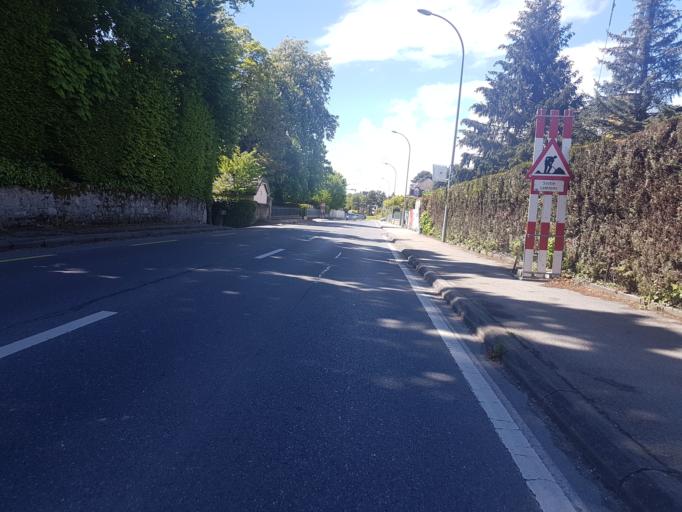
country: CH
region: Vaud
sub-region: Nyon District
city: Prangins
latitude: 46.3894
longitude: 6.2497
